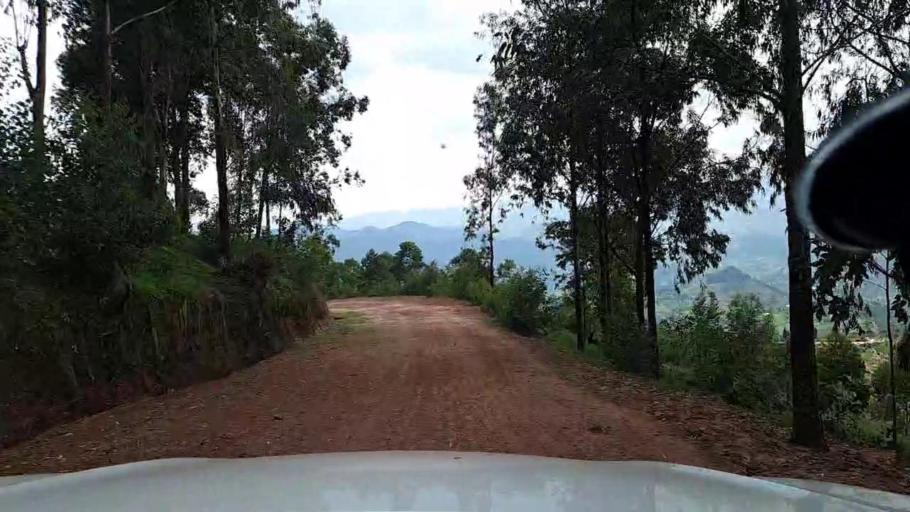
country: RW
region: Southern Province
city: Gitarama
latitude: -1.8394
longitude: 29.8236
